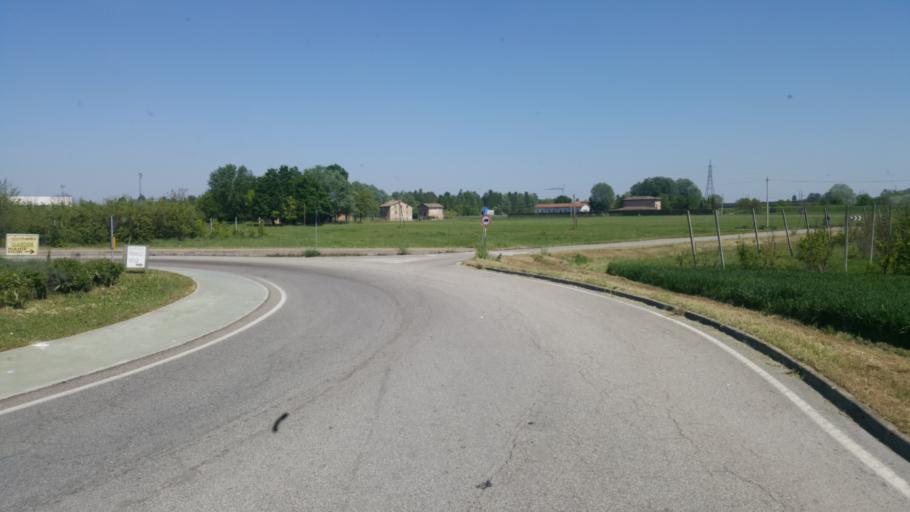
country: IT
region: Emilia-Romagna
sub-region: Provincia di Modena
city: Campogalliano
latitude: 44.6815
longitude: 10.8560
